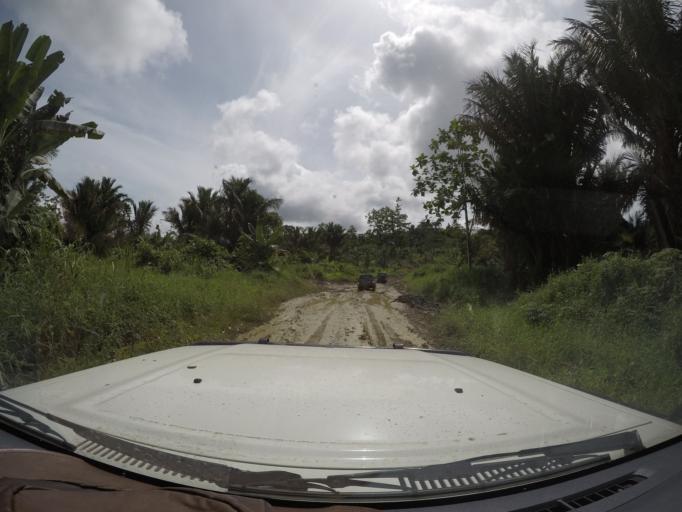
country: PG
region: Gulf
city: Kerema
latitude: -7.9957
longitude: 145.8293
